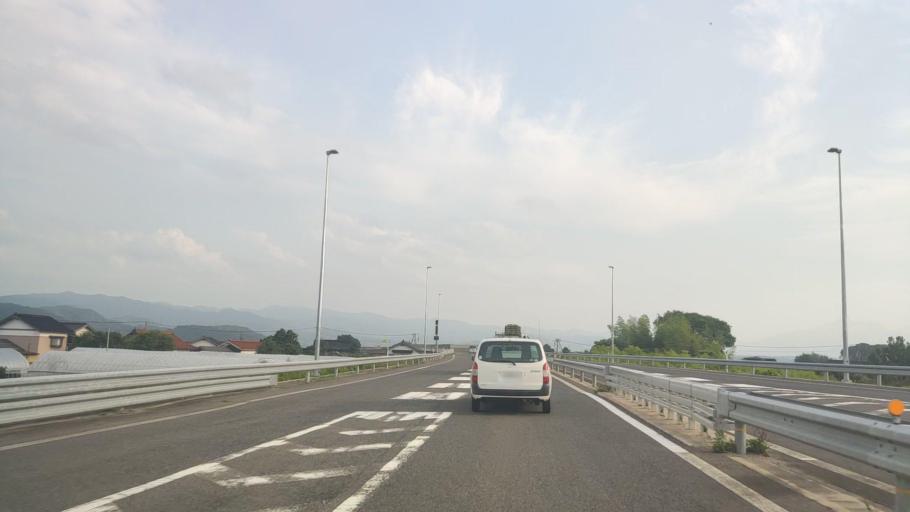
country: JP
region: Tottori
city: Kurayoshi
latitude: 35.4449
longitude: 133.8074
